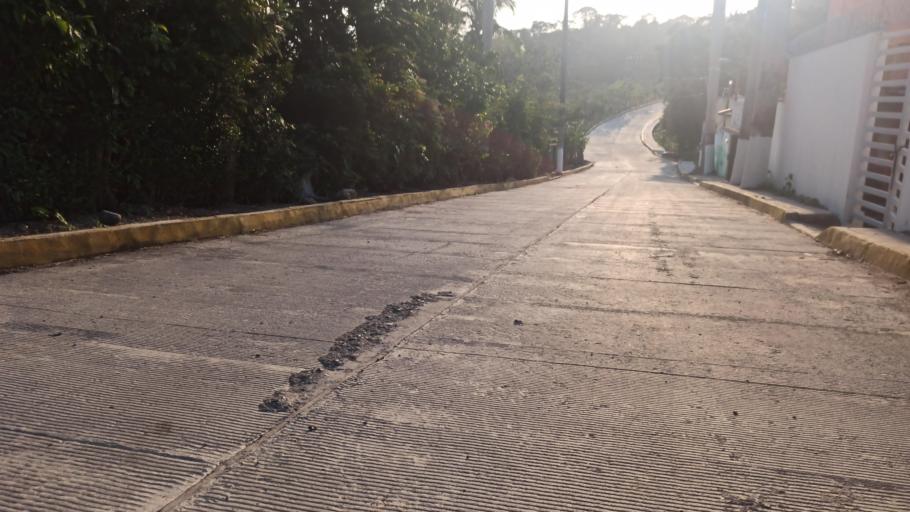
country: MX
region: Veracruz
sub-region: Poza Rica de Hidalgo
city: Arroyo del Maiz Uno
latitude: 20.4786
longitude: -97.3858
